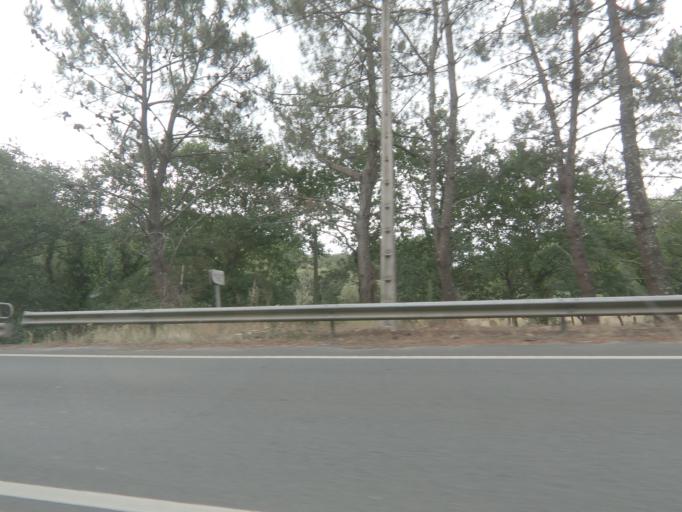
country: PT
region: Viana do Castelo
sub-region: Valenca
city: Valenca
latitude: 41.9949
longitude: -8.6914
